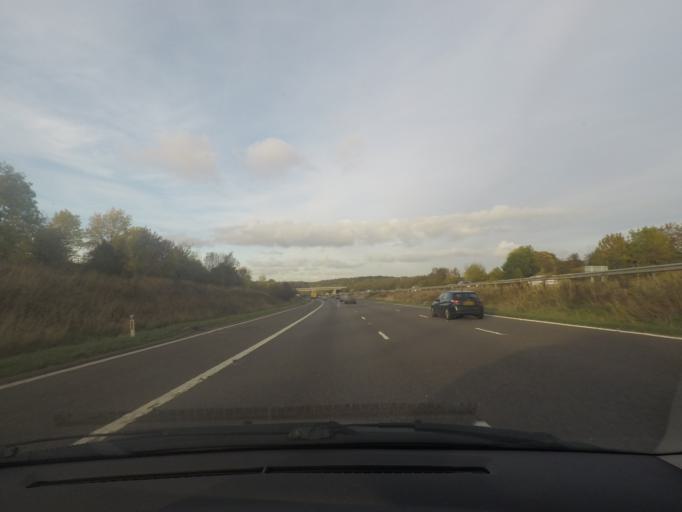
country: GB
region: England
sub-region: City and Borough of Wakefield
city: Crigglestone
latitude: 53.6265
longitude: -1.5431
